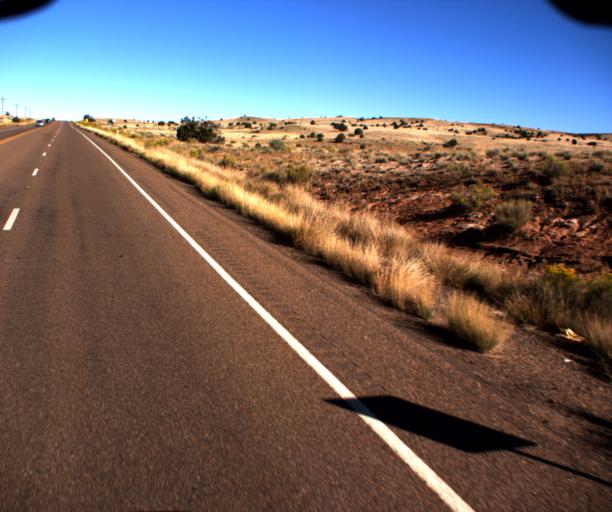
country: US
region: Arizona
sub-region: Navajo County
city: Taylor
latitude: 34.4253
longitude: -110.0891
